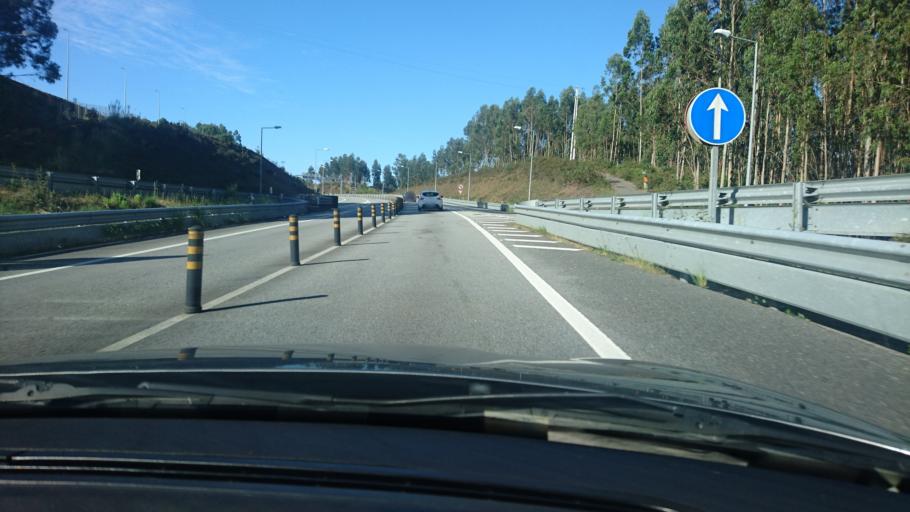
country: PT
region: Aveiro
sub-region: Santa Maria da Feira
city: Arrifana
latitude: 40.9236
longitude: -8.4891
